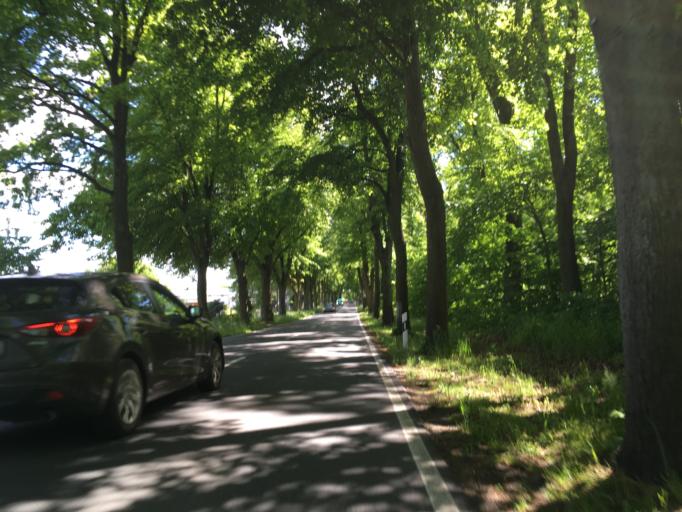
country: DE
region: Brandenburg
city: Ahrensfelde
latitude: 52.6230
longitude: 13.6116
